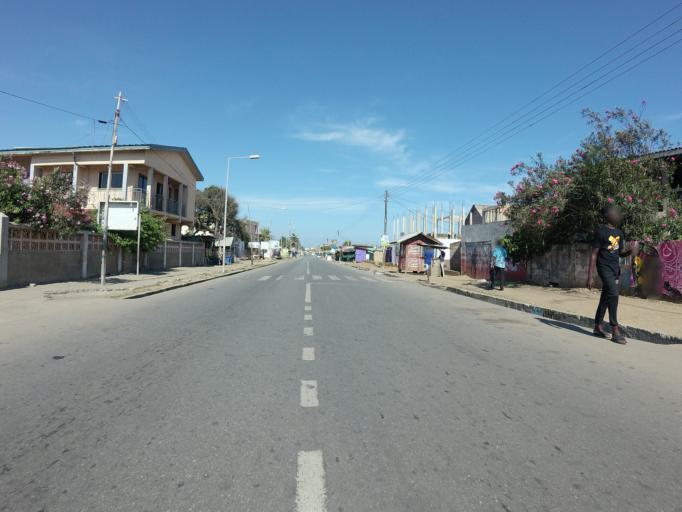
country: GH
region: Greater Accra
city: Accra
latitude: 5.5617
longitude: -0.1519
